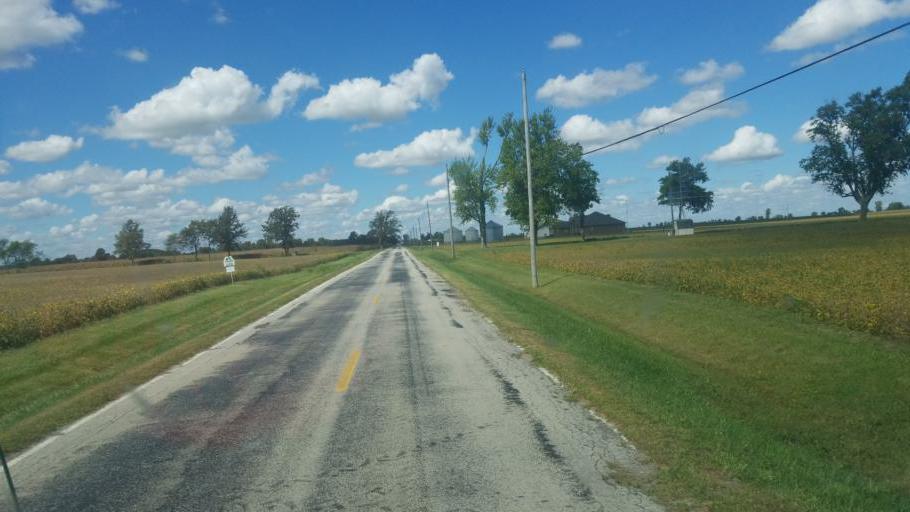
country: US
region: Ohio
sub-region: Madison County
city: West Jefferson
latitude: 39.9968
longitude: -83.3469
